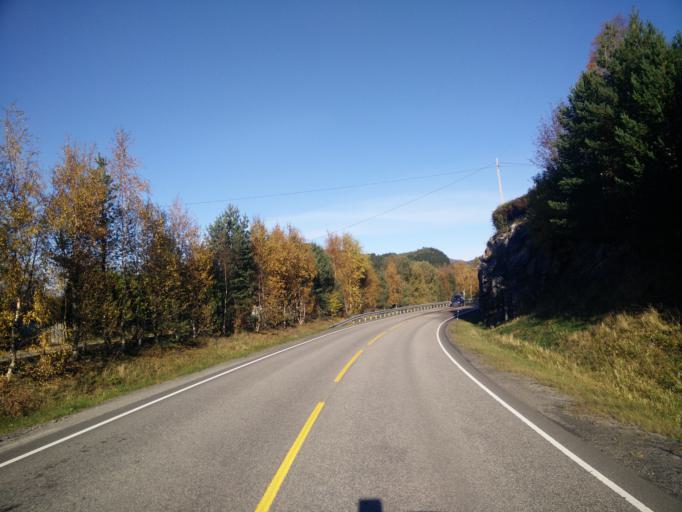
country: NO
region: More og Romsdal
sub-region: Kristiansund
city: Rensvik
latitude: 63.0156
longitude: 8.0029
